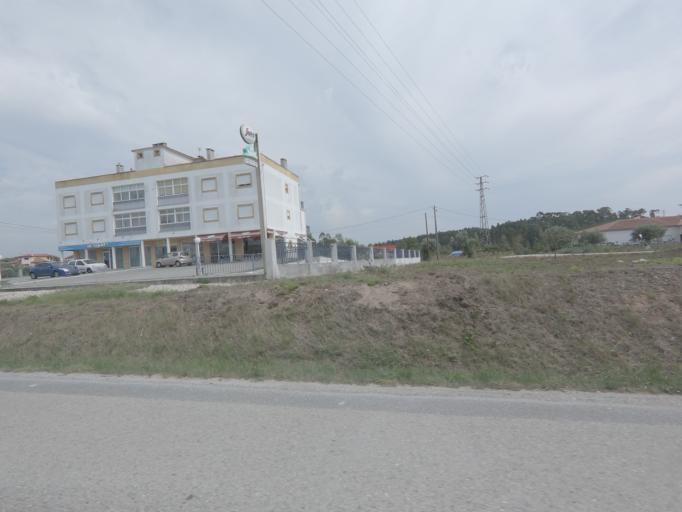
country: PT
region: Leiria
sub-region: Pombal
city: Pombal
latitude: 39.8706
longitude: -8.6920
